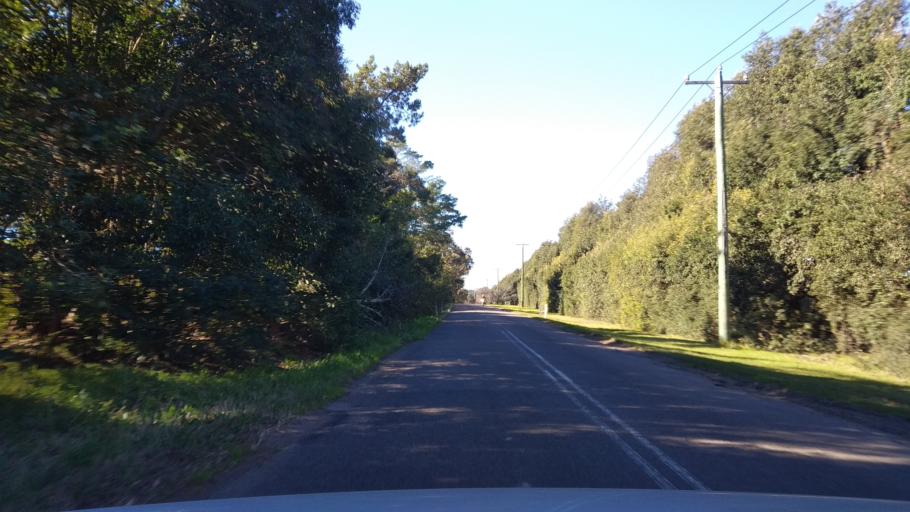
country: AU
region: New South Wales
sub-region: Wyong Shire
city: Little Jilliby
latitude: -33.2382
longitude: 151.2318
